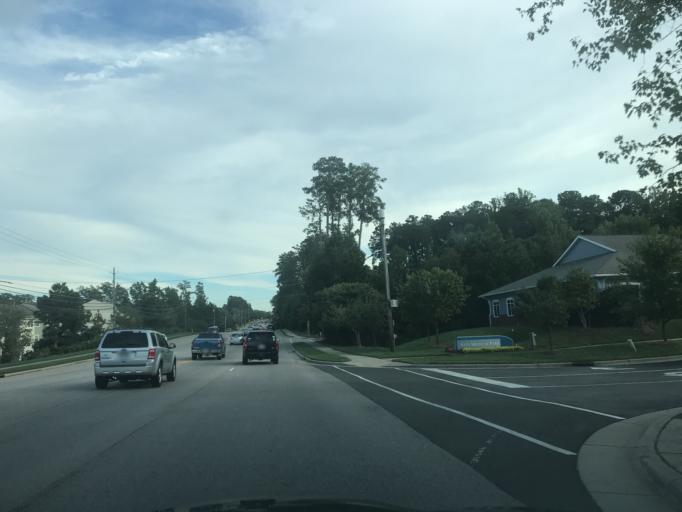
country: US
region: North Carolina
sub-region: Wake County
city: Apex
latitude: 35.7417
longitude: -78.8686
